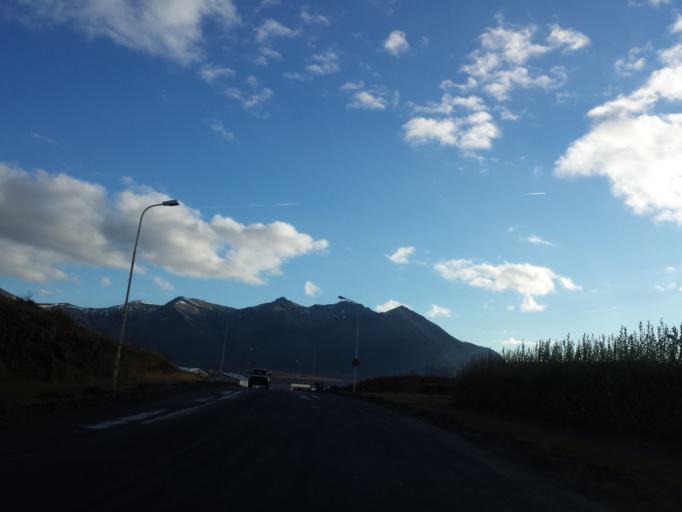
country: IS
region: West
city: Borgarnes
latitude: 64.5482
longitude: -21.9107
